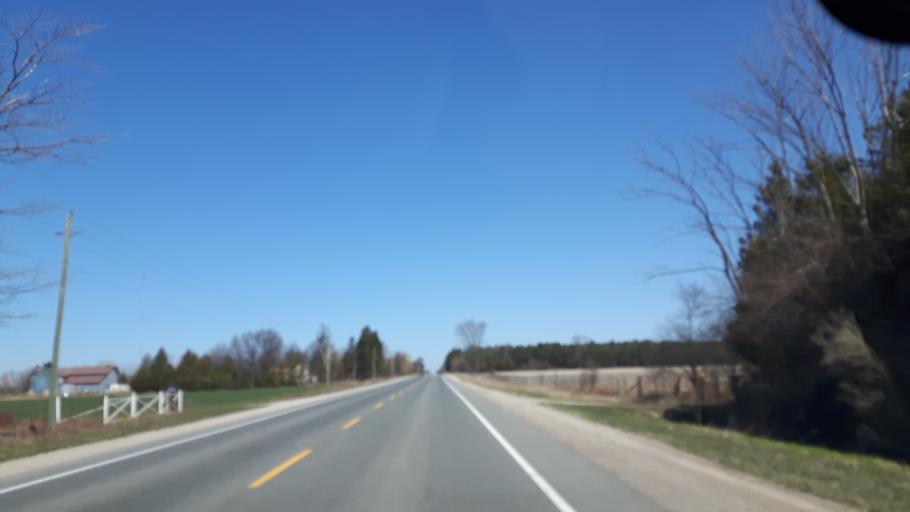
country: CA
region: Ontario
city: Goderich
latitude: 43.6719
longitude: -81.7056
